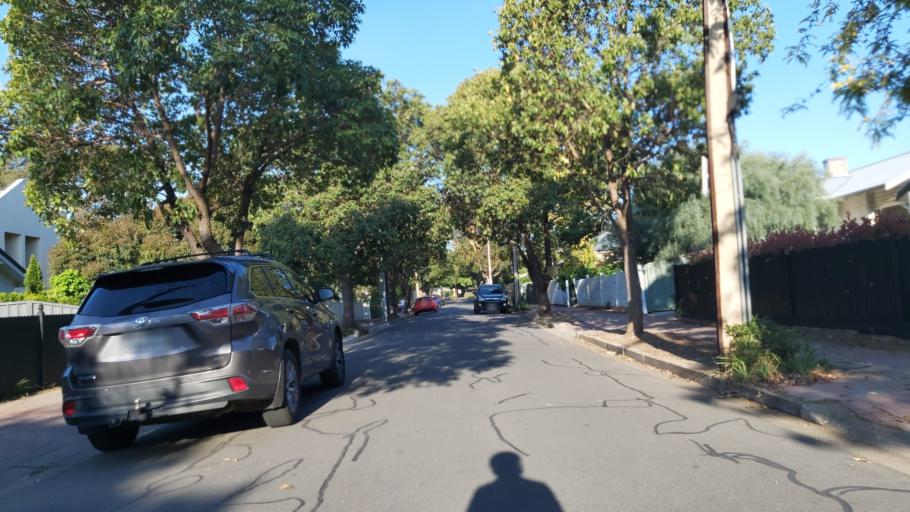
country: AU
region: South Australia
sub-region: Unley
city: Fullarton
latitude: -34.9527
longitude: 138.6274
